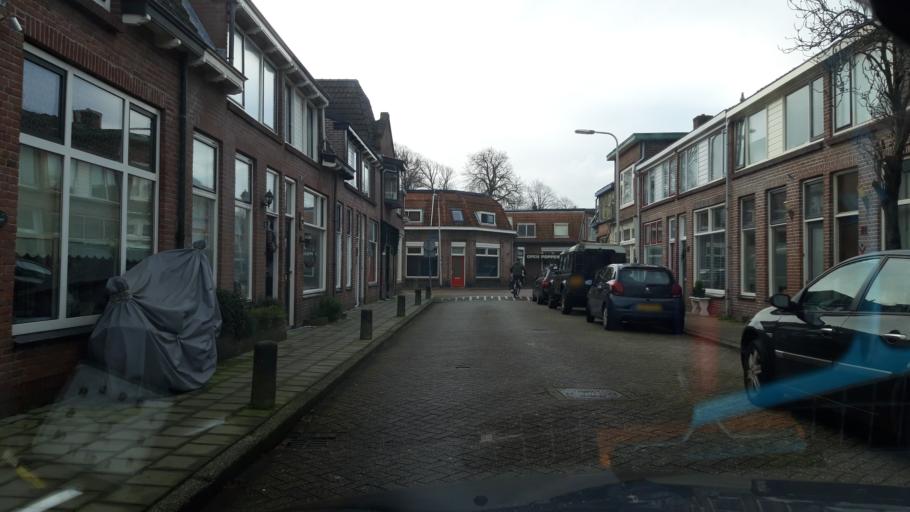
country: NL
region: South Holland
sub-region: Gemeente Hillegom
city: Hillegom
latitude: 52.2923
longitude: 4.5807
